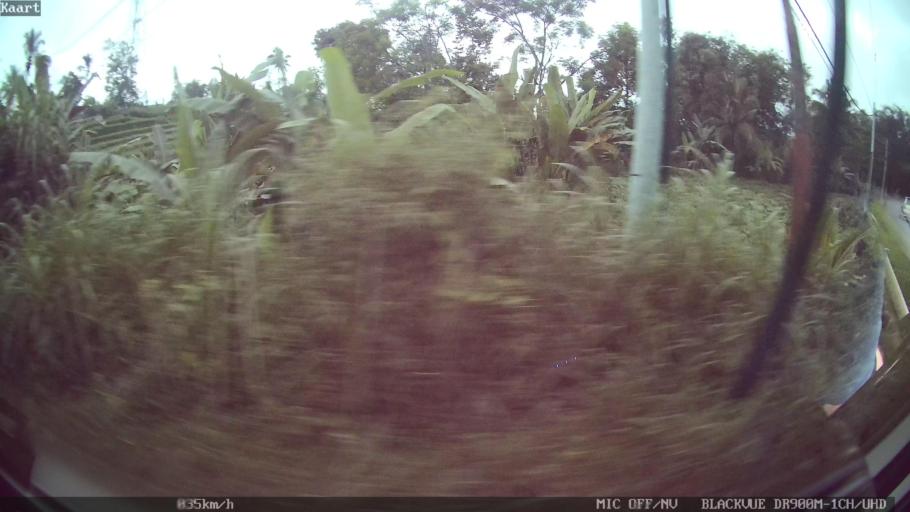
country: ID
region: Bali
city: Peneng
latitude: -8.3407
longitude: 115.1874
